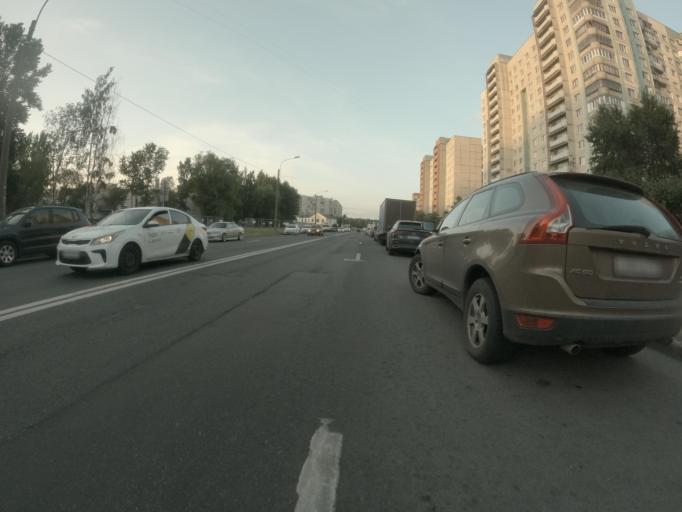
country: RU
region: St.-Petersburg
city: Krasnogvargeisky
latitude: 59.9547
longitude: 30.4849
